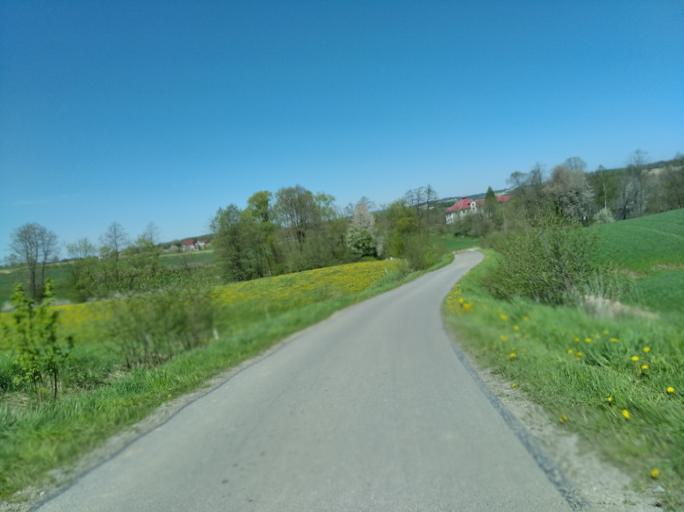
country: PL
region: Subcarpathian Voivodeship
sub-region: Powiat ropczycko-sedziszowski
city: Wielopole Skrzynskie
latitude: 49.9134
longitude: 21.5484
